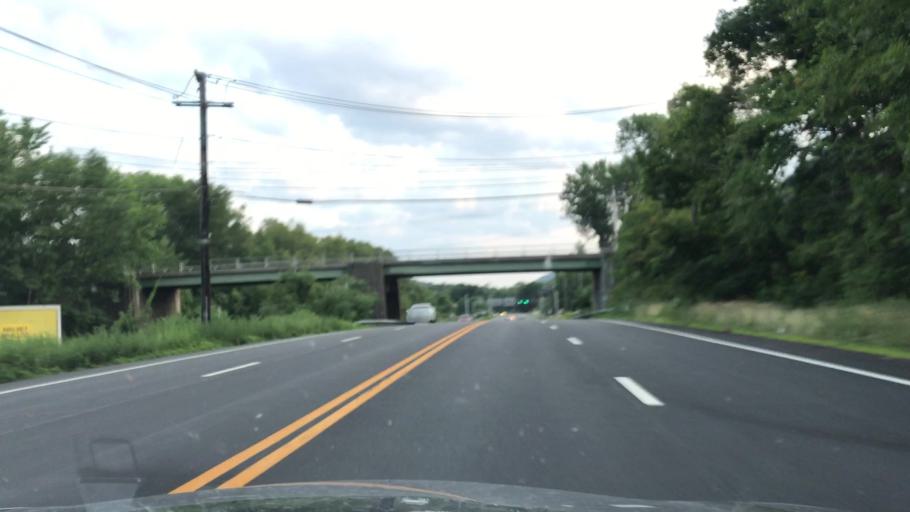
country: US
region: New York
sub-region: Rockland County
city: Sloatsburg
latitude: 41.2293
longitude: -74.1840
